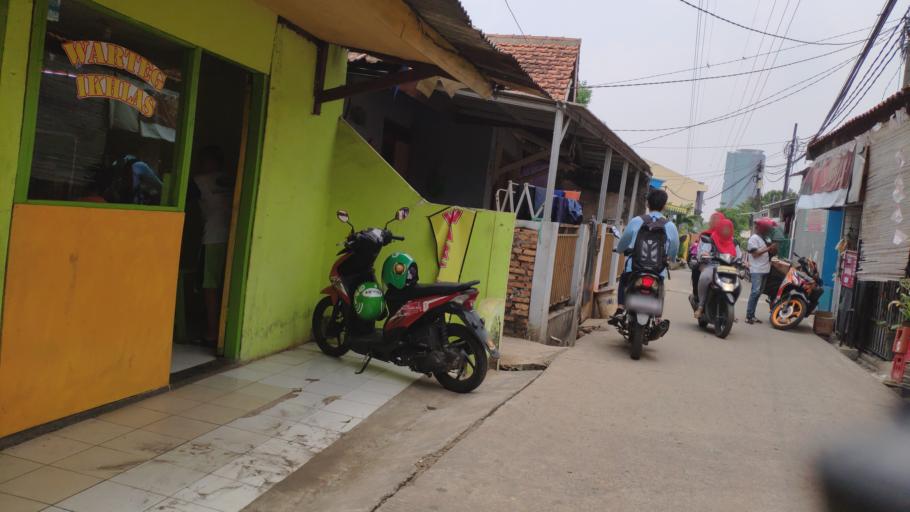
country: ID
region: West Java
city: Depok
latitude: -6.3080
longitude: 106.8318
